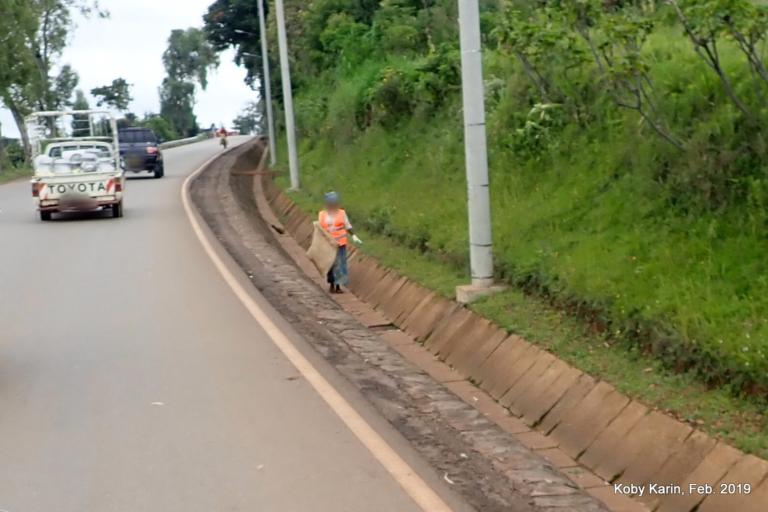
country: RW
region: Kigali
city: Kigali
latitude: -1.8543
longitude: 29.9760
